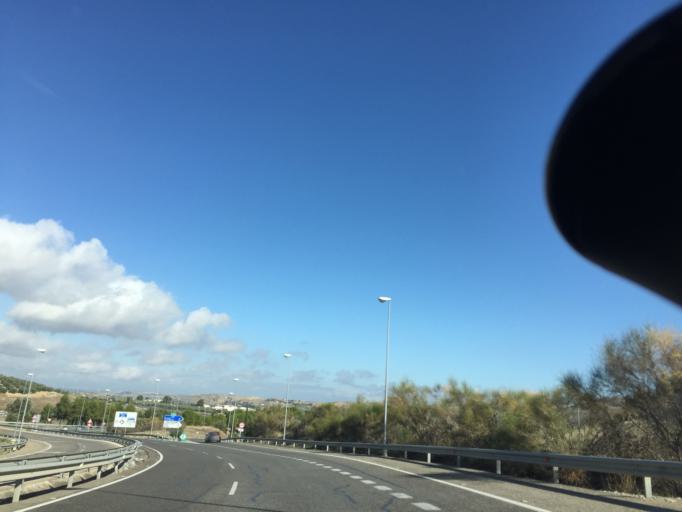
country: ES
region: Andalusia
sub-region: Provincia de Jaen
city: Jaen
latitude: 37.7790
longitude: -3.7559
